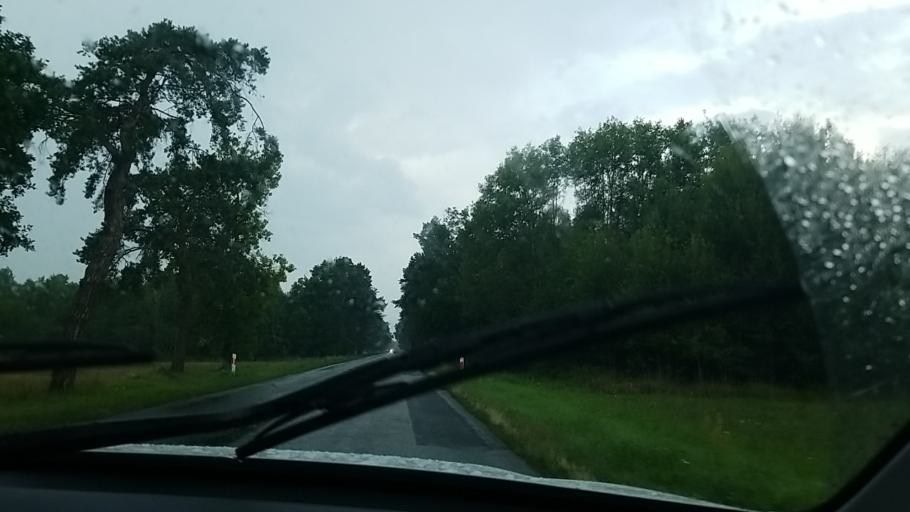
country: PL
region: Lublin Voivodeship
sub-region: Powiat leczynski
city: Cycow
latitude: 51.3387
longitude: 23.1559
